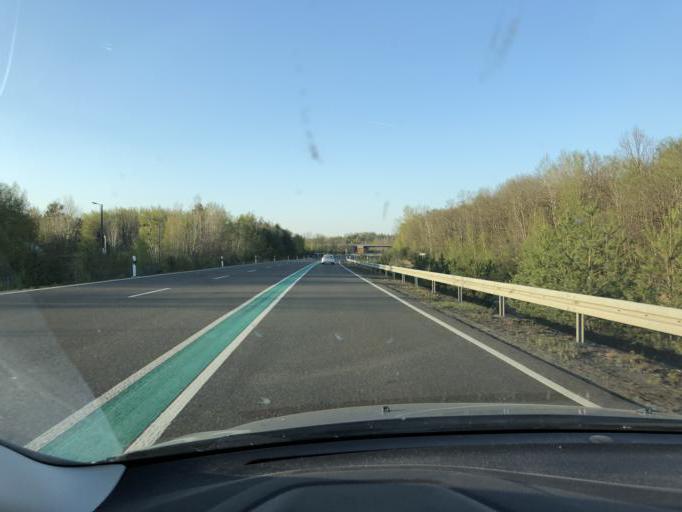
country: DE
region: Brandenburg
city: Senftenberg
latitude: 51.5220
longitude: 13.9637
